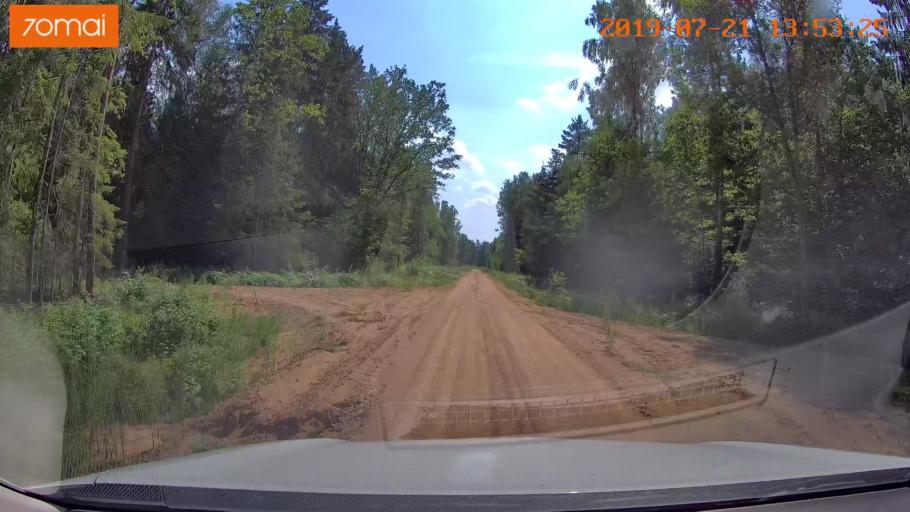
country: BY
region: Grodnenskaya
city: Lyubcha
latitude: 53.7796
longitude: 26.0633
